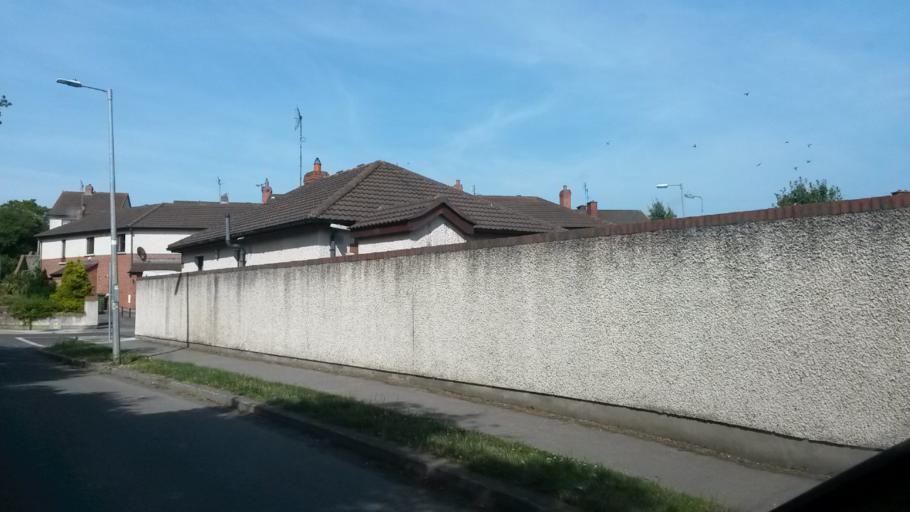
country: IE
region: Leinster
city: Lusk
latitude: 53.5280
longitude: -6.1756
